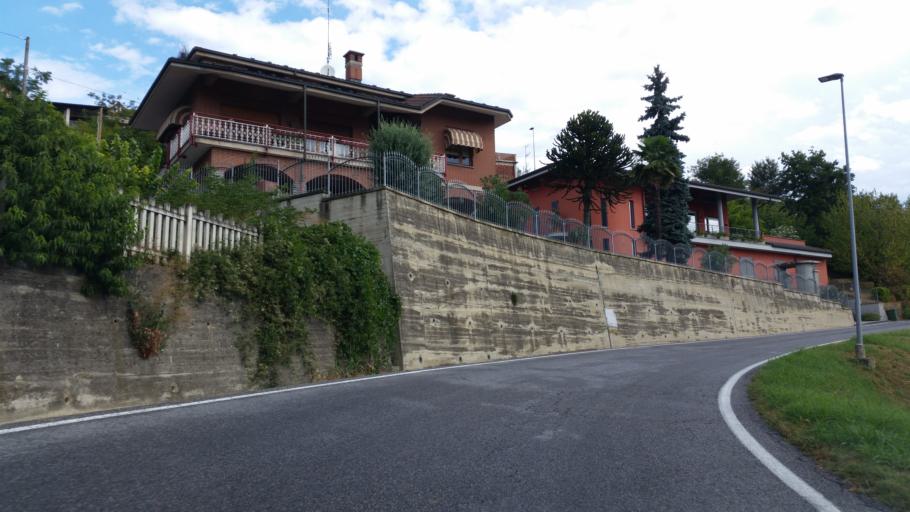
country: IT
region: Piedmont
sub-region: Provincia di Cuneo
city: Castagnito
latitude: 44.7522
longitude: 8.0495
